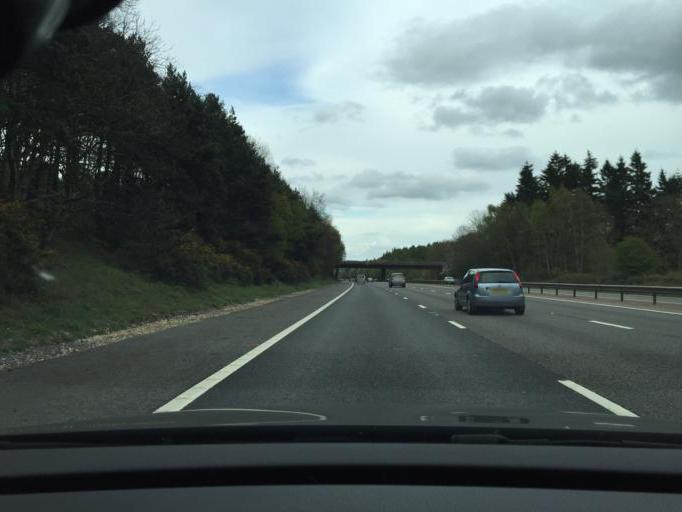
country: GB
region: England
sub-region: West Berkshire
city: Hermitage
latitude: 51.4635
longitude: -1.2525
